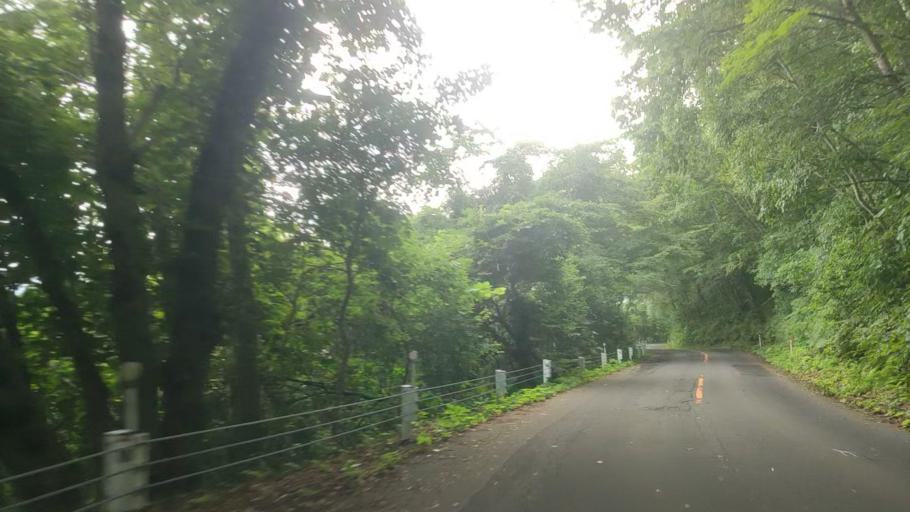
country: JP
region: Hokkaido
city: Hakodate
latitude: 41.7628
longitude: 140.7049
